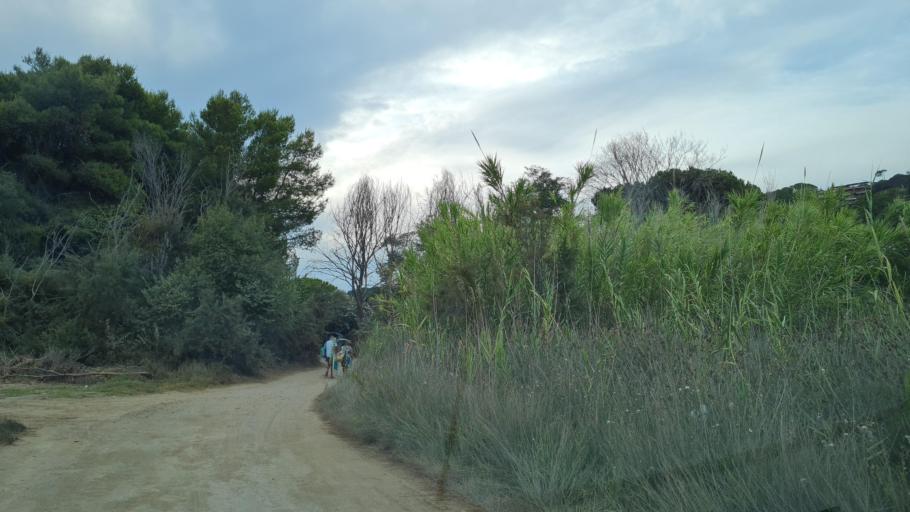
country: IT
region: Tuscany
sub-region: Provincia di Grosseto
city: Porto Ercole
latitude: 42.4035
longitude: 11.2060
